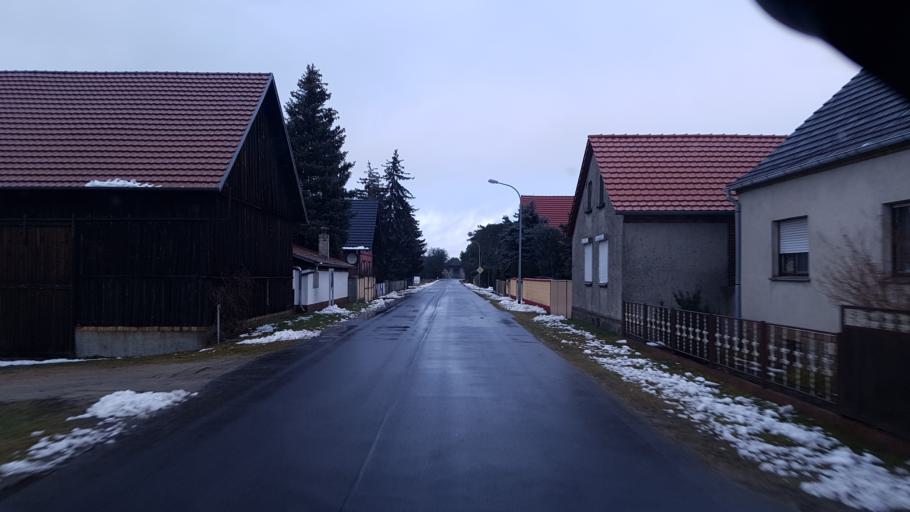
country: DE
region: Brandenburg
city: Janschwalde
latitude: 51.8658
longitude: 14.5092
